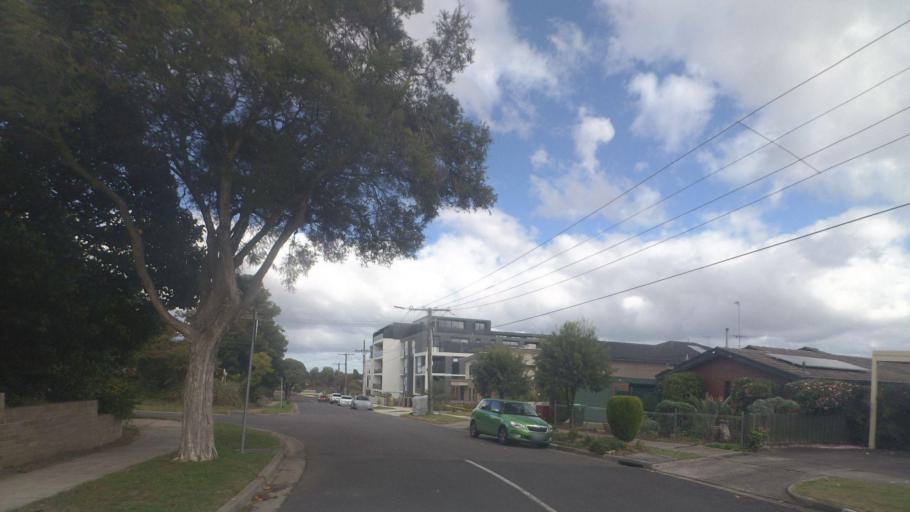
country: AU
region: Victoria
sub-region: Whitehorse
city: Vermont South
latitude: -37.8545
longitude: 145.1767
